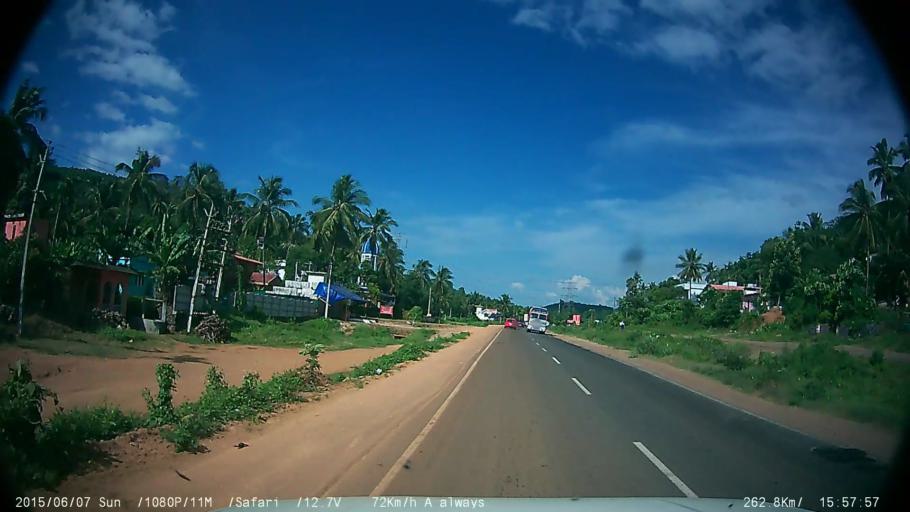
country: IN
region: Kerala
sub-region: Thrissur District
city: Chelakara
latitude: 10.5768
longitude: 76.3951
